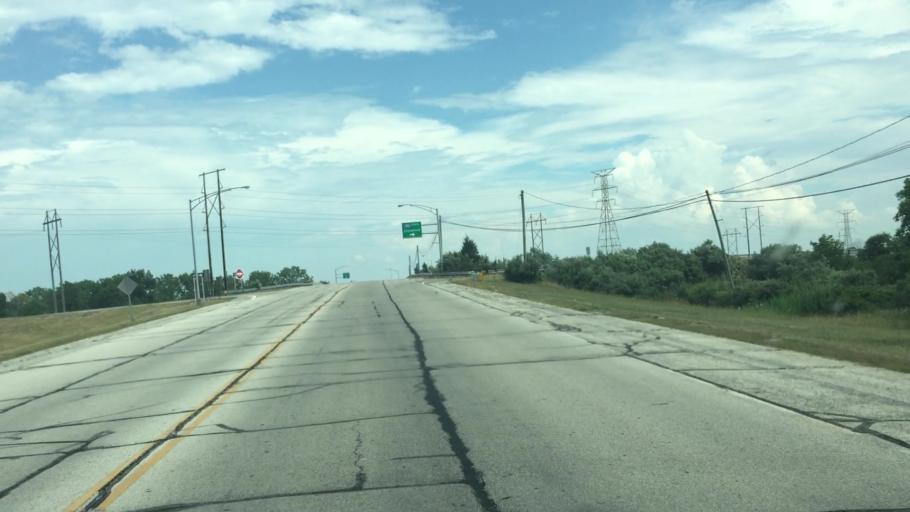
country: US
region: Ohio
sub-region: Wood County
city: Walbridge
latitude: 41.5879
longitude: -83.4797
